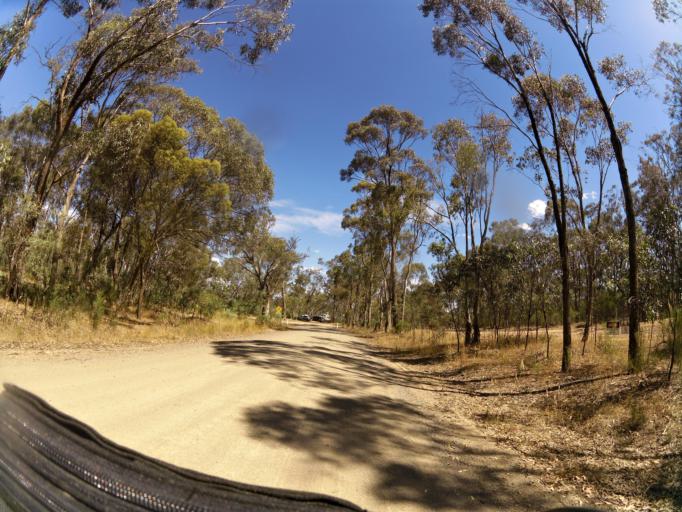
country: AU
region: Victoria
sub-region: Campaspe
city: Kyabram
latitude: -36.8546
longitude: 145.0668
